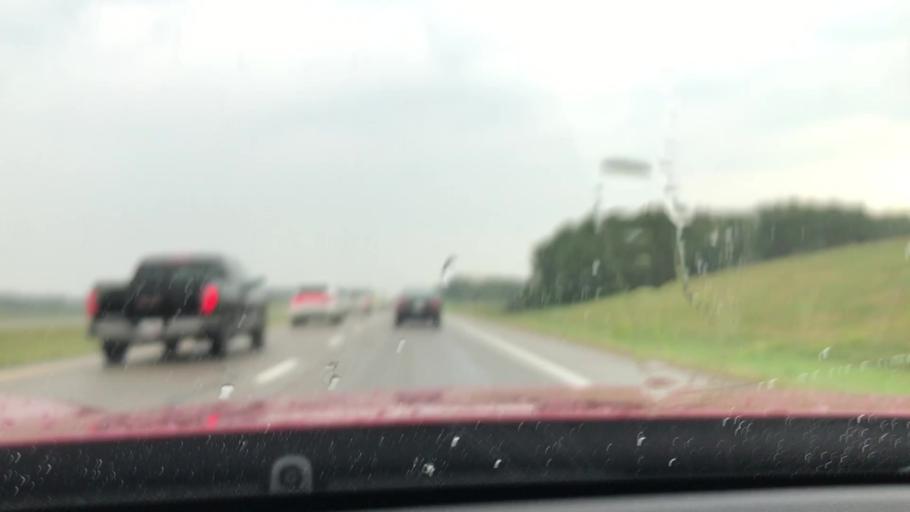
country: CA
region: Alberta
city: Ponoka
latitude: 52.7293
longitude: -113.6436
